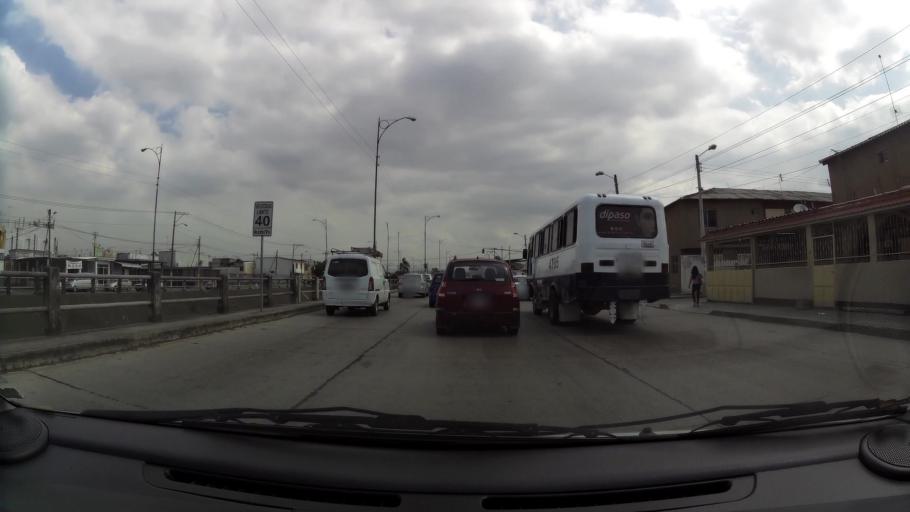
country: EC
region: Guayas
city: Eloy Alfaro
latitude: -2.0863
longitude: -79.9229
